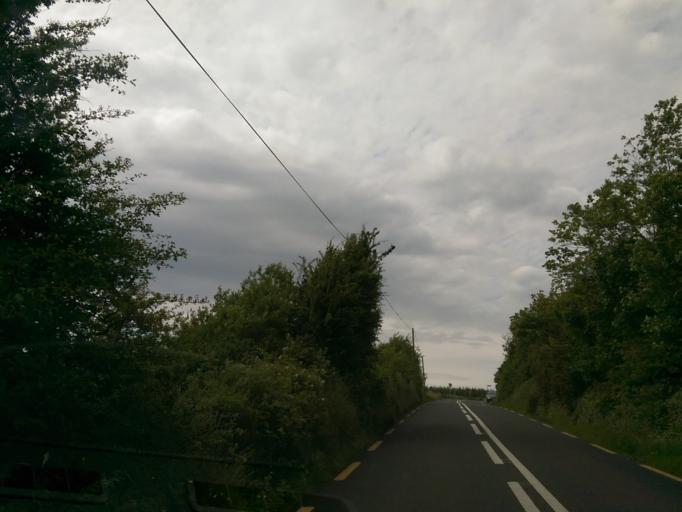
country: IE
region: Connaught
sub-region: County Galway
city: Bearna
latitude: 52.9950
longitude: -9.3053
